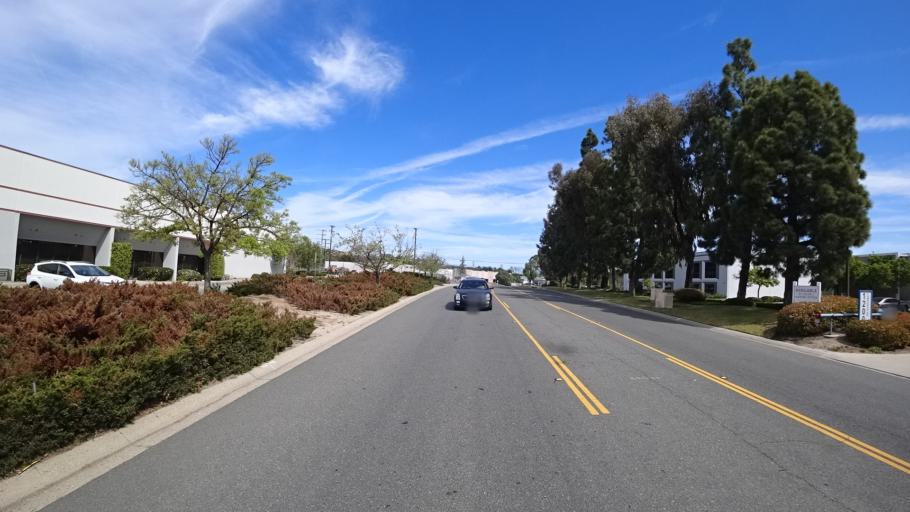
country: US
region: California
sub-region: Ventura County
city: Casa Conejo
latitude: 34.1947
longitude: -118.9300
